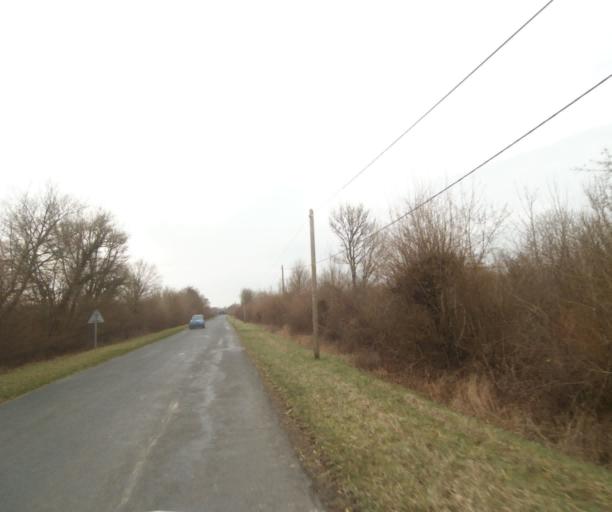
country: FR
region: Champagne-Ardenne
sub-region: Departement de la Haute-Marne
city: Villiers-en-Lieu
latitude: 48.6531
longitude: 4.8759
